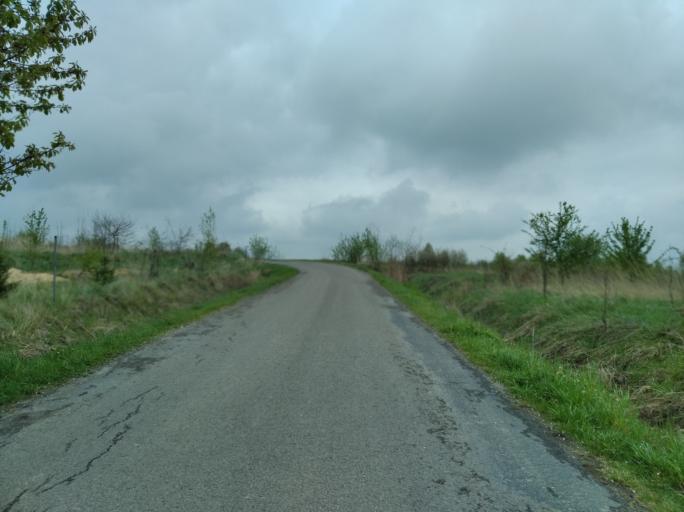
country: PL
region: Subcarpathian Voivodeship
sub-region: Powiat brzozowski
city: Golcowa
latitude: 49.7522
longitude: 22.0435
